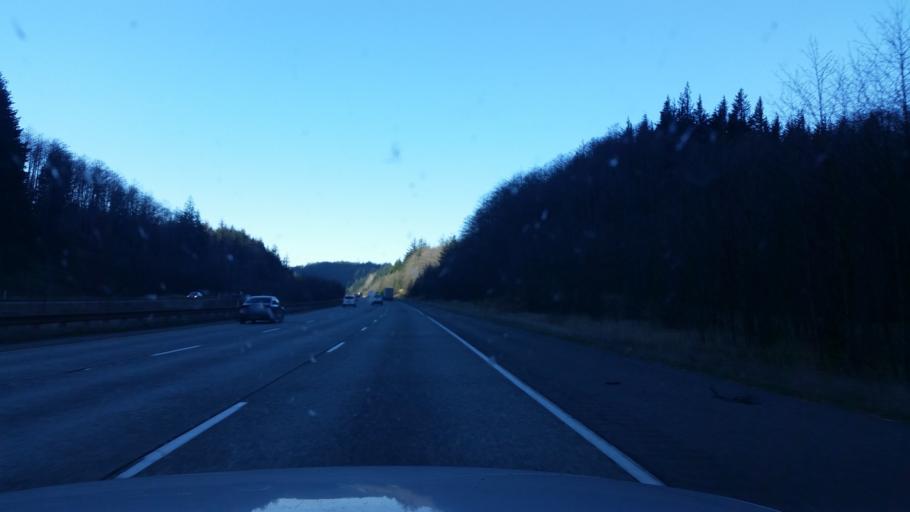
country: US
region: Washington
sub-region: King County
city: Tanner
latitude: 47.4337
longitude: -121.6405
